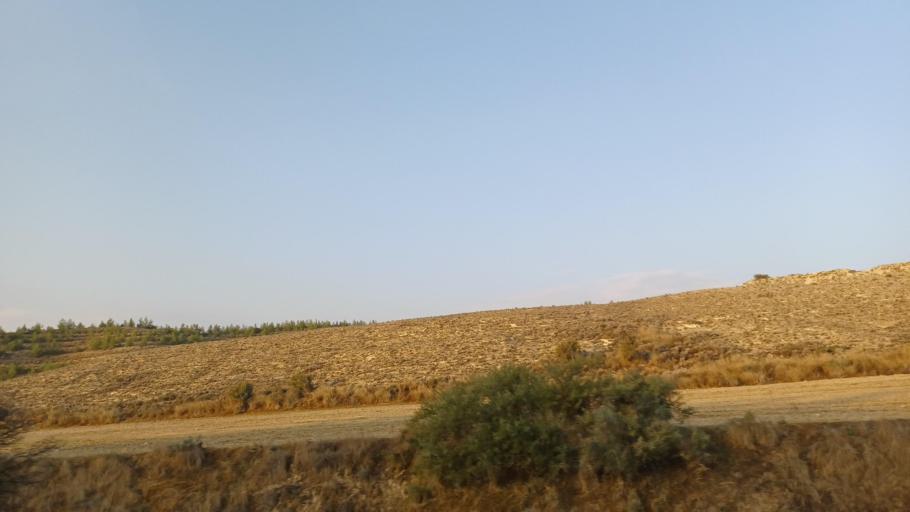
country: CY
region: Larnaka
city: Athienou
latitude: 35.0045
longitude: 33.5246
